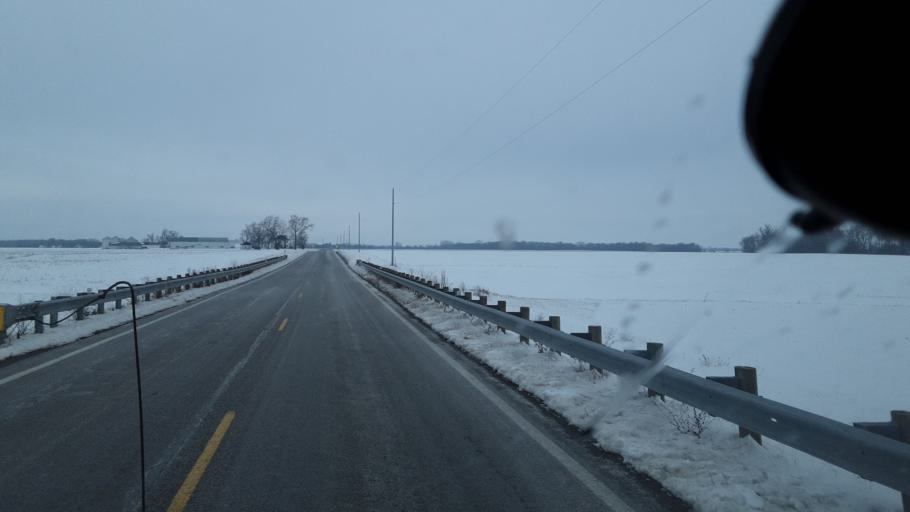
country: US
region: Ohio
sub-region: Champaign County
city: Mechanicsburg
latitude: 40.1175
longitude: -83.4318
